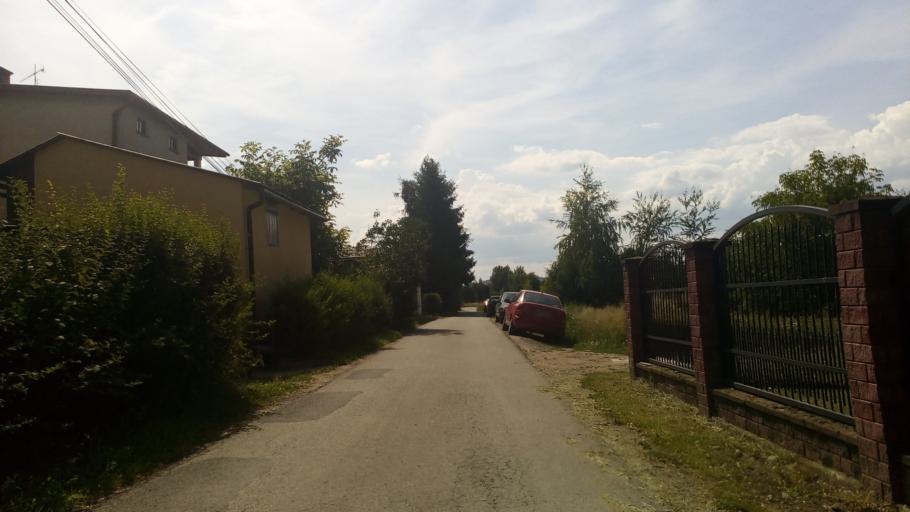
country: PL
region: Lesser Poland Voivodeship
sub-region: Powiat nowosadecki
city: Stary Sacz
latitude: 49.5694
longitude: 20.6317
